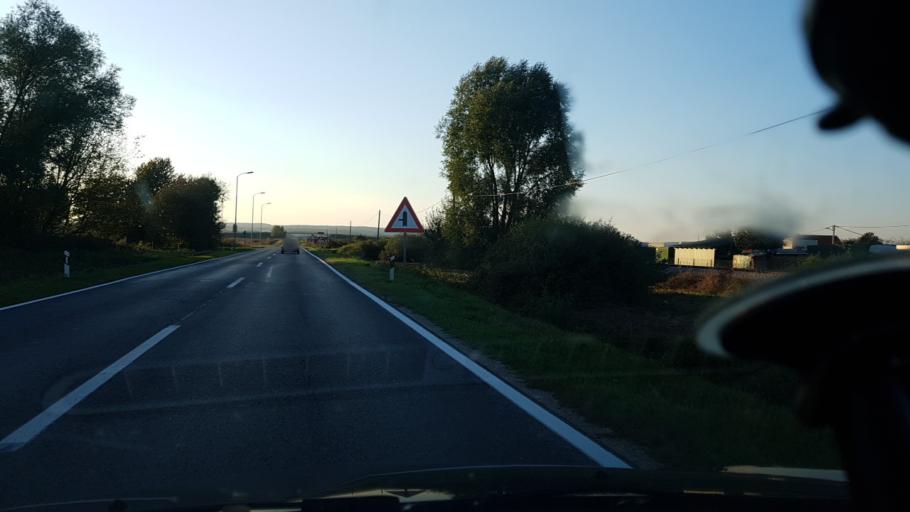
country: HR
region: Koprivnicko-Krizevacka
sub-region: Grad Koprivnica
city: Koprivnica
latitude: 46.1393
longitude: 16.8486
